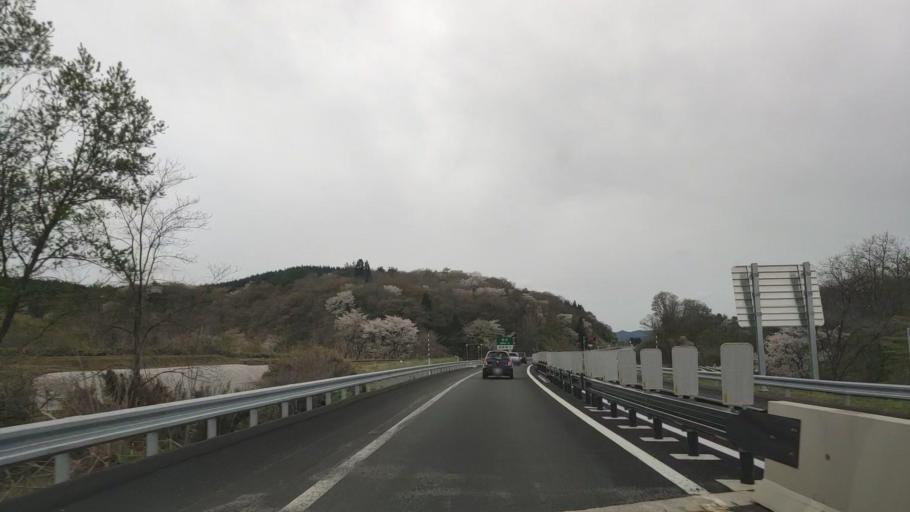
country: JP
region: Akita
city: Takanosu
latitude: 40.2060
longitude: 140.3248
